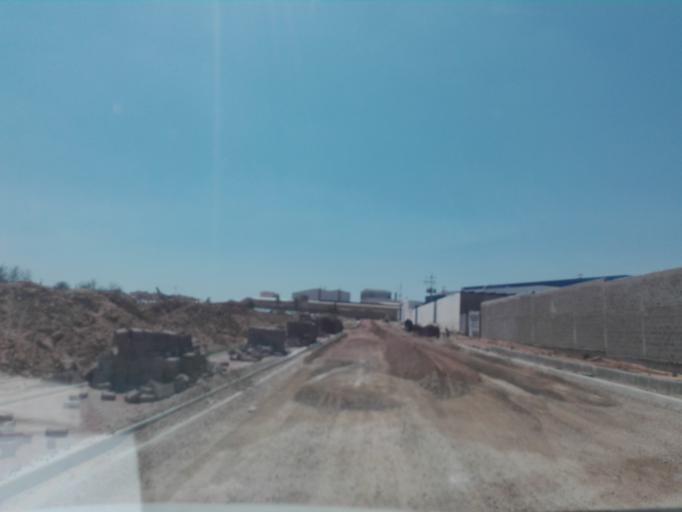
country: TN
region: Safaqis
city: Sfax
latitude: 34.7272
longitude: 10.5169
